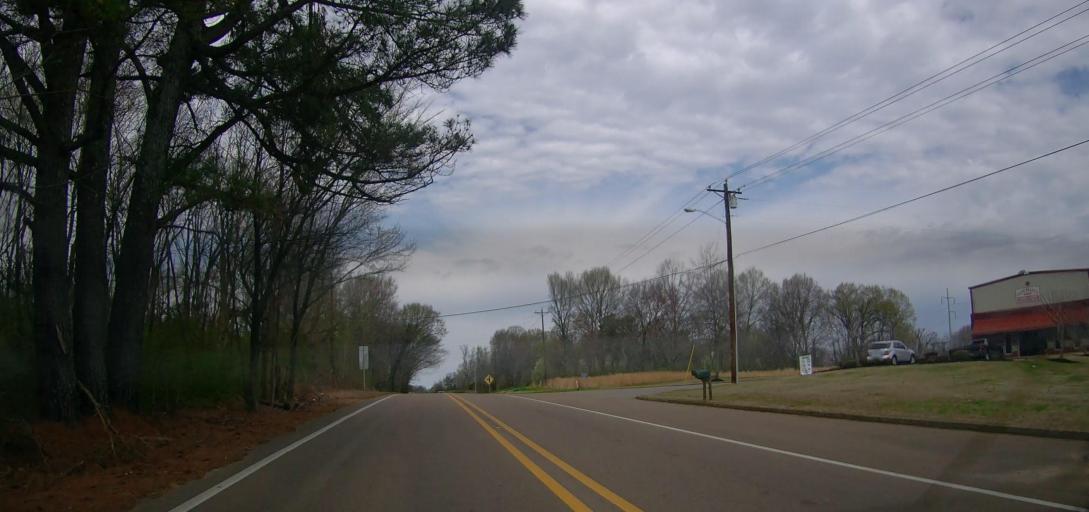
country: US
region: Mississippi
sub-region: De Soto County
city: Olive Branch
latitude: 34.9712
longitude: -89.8388
